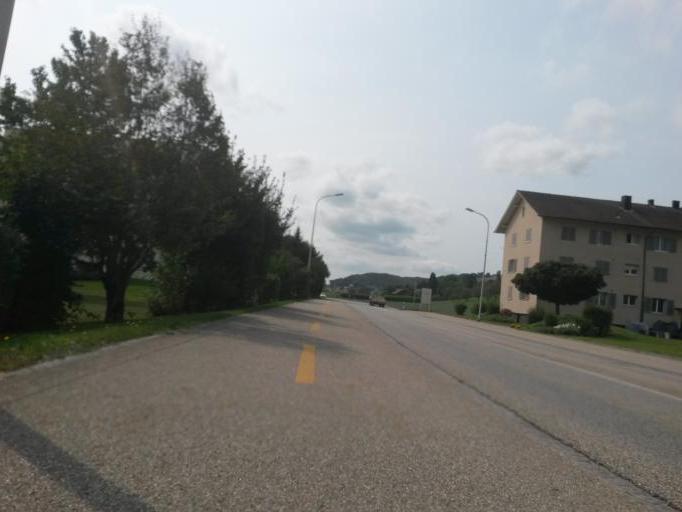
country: CH
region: Solothurn
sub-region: Bezirk Gaeu
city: Oensingen
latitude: 47.2842
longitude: 7.7045
